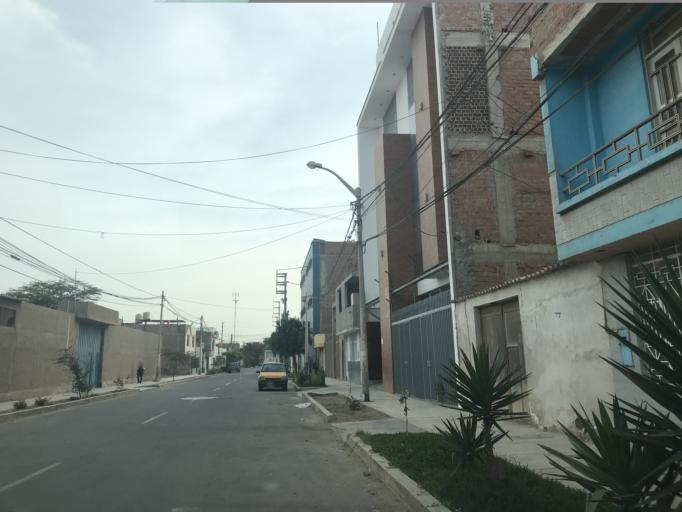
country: PE
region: Lambayeque
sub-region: Provincia de Chiclayo
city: Chiclayo
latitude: -6.7913
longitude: -79.8454
